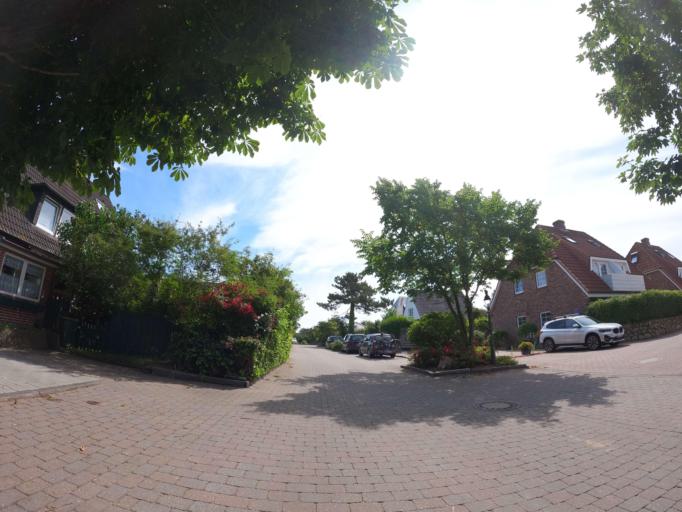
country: DE
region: Schleswig-Holstein
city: Westerland
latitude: 54.9180
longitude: 8.3156
